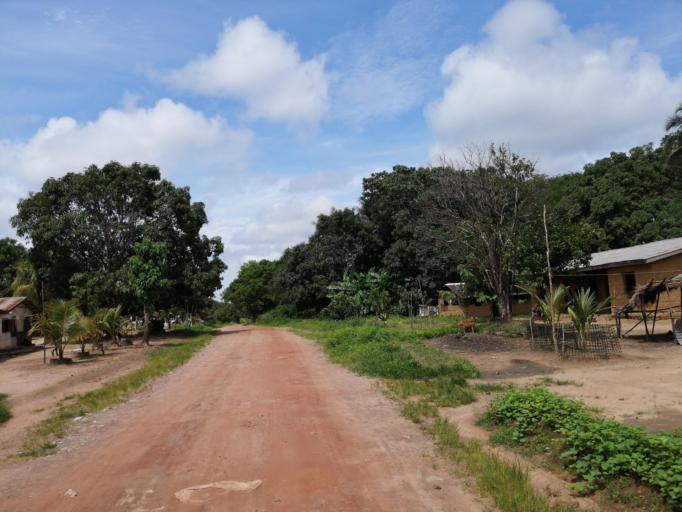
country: SL
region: Northern Province
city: Pepel
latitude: 8.6871
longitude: -12.9983
